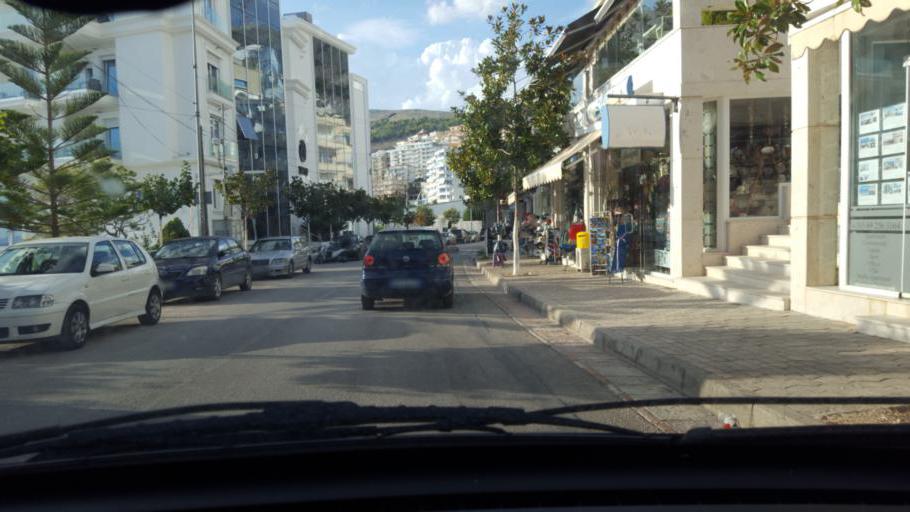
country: AL
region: Vlore
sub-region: Rrethi i Sarandes
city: Sarande
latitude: 39.8691
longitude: 20.0145
